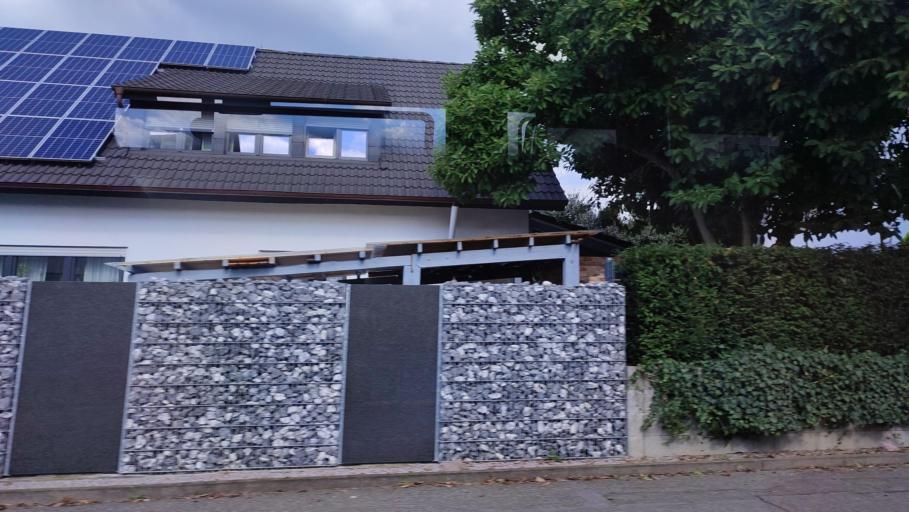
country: DE
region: Baden-Wuerttemberg
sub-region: Freiburg Region
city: Oberkirch
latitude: 48.5326
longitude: 8.0734
